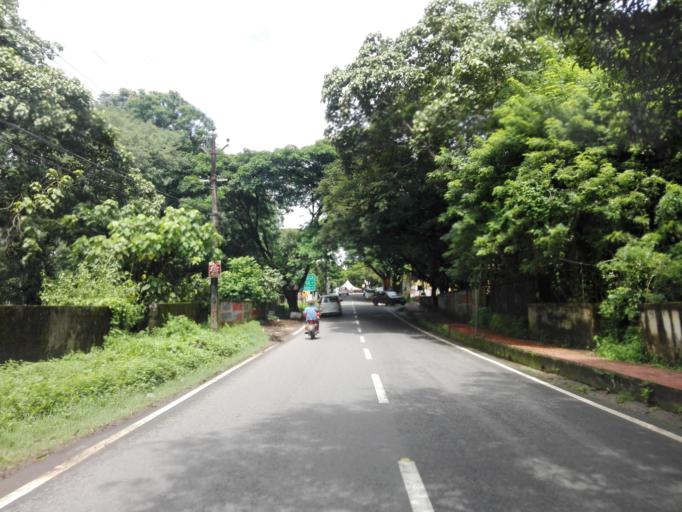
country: IN
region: Kerala
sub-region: Ernakulam
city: Elur
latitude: 10.0211
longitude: 76.3359
